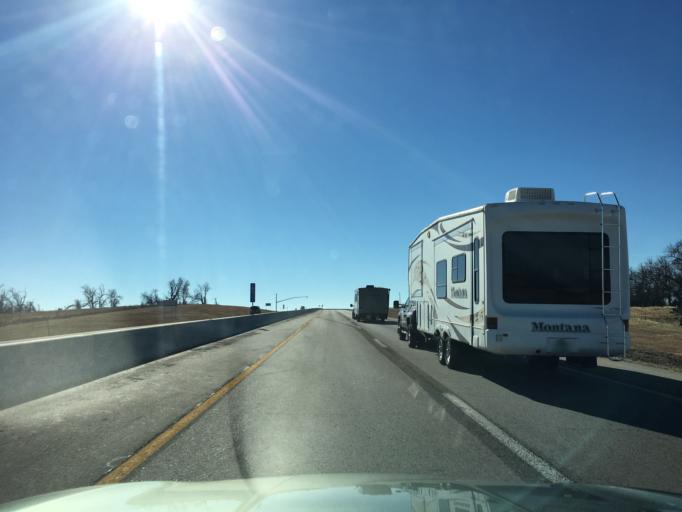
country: US
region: Oklahoma
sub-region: Kay County
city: Blackwell
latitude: 37.0052
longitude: -97.3408
